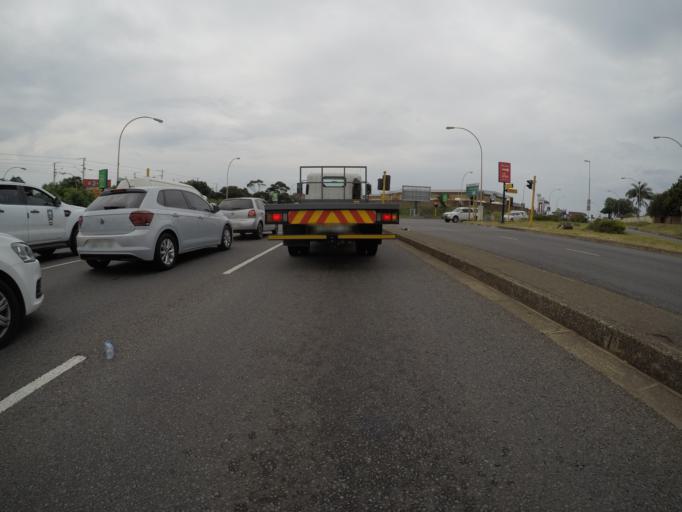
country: ZA
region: Eastern Cape
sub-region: Buffalo City Metropolitan Municipality
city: East London
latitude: -32.9845
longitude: 27.8971
